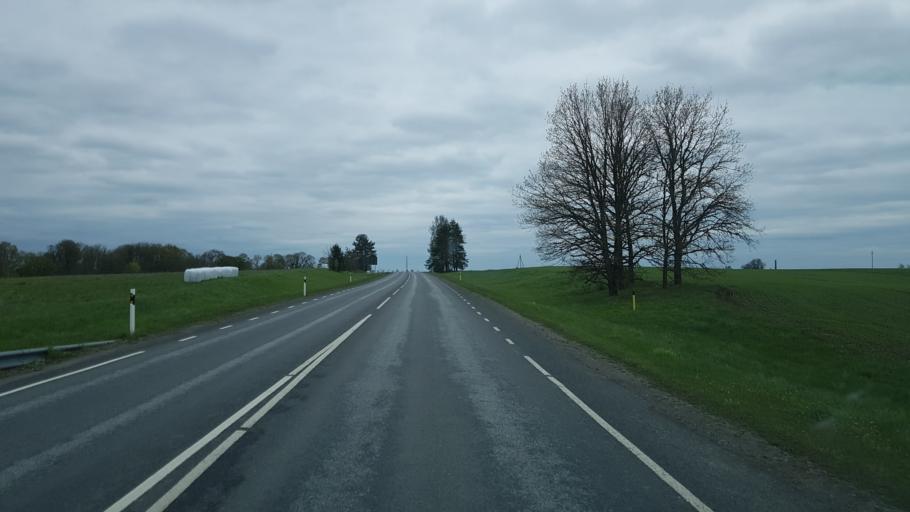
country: EE
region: Viljandimaa
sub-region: Viljandi linn
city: Viljandi
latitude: 58.4011
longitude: 25.5917
